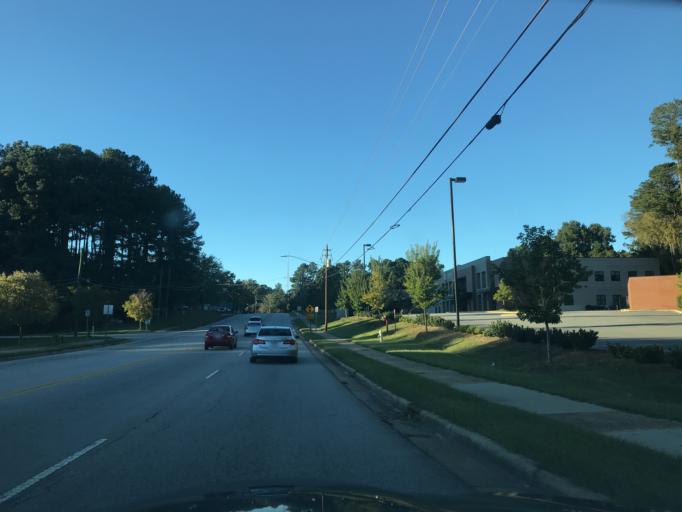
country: US
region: North Carolina
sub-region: Wake County
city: Raleigh
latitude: 35.7657
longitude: -78.6155
